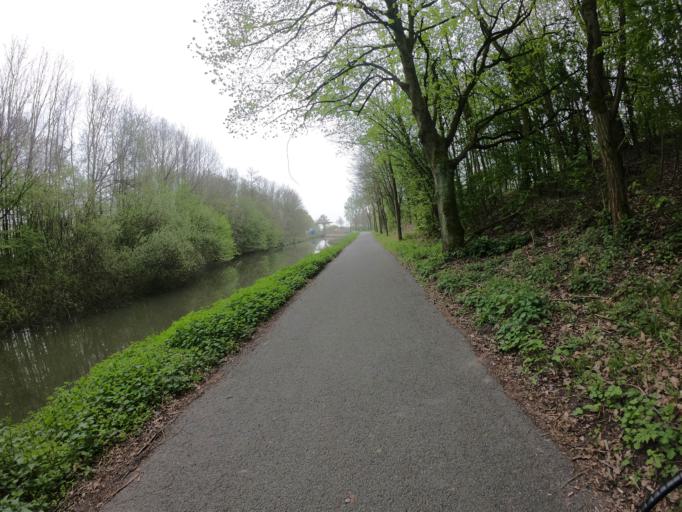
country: BE
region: Flanders
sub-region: Provincie West-Vlaanderen
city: Zwevegem
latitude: 50.7799
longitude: 3.3783
